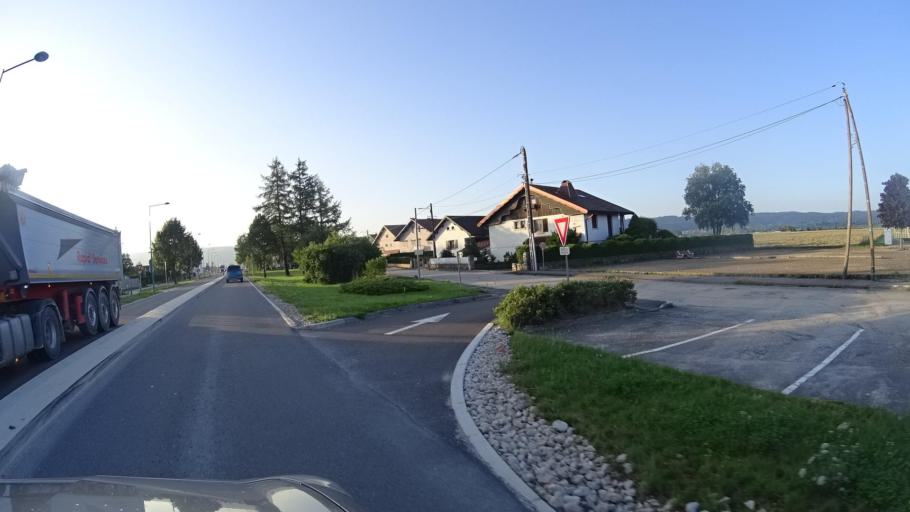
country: FR
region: Franche-Comte
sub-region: Departement du Doubs
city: Doubs
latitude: 46.9147
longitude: 6.3155
